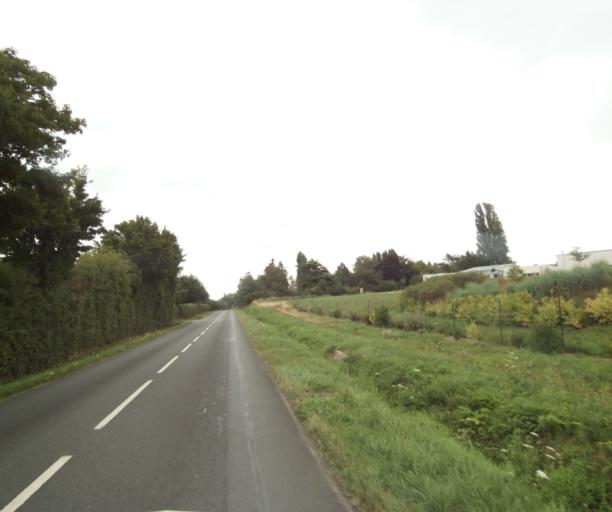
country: FR
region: Pays de la Loire
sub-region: Departement de la Sarthe
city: Solesmes
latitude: 47.8473
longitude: -0.3127
